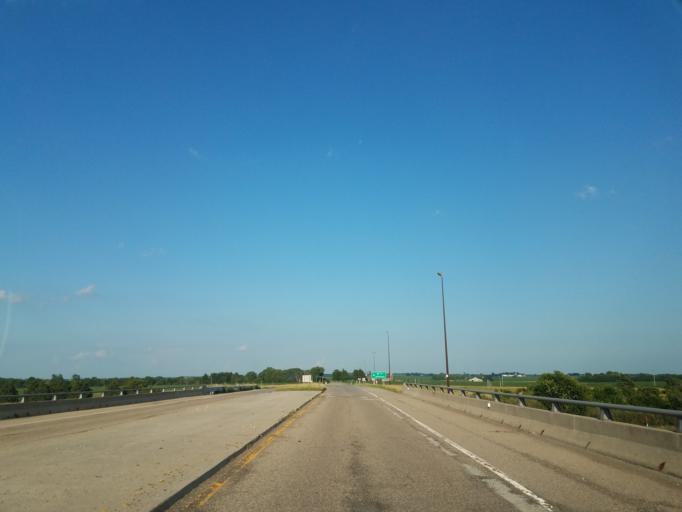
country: US
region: Illinois
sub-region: McLean County
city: Twin Grove
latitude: 40.4082
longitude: -89.0543
